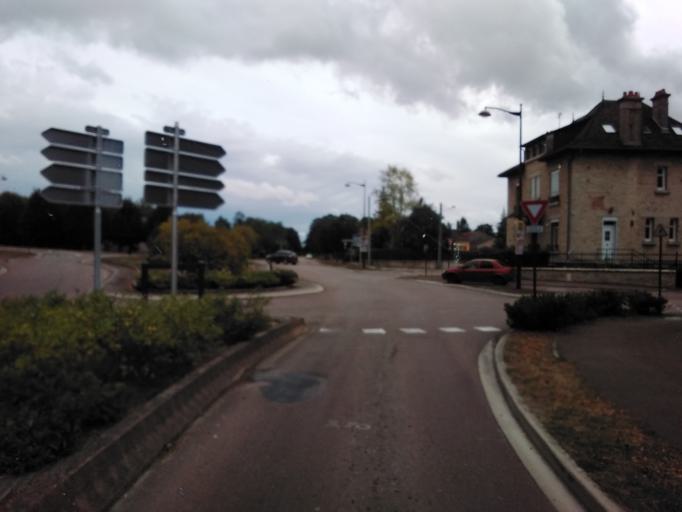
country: FR
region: Champagne-Ardenne
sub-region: Departement de l'Aube
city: Brienne-le-Chateau
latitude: 48.3922
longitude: 4.5299
